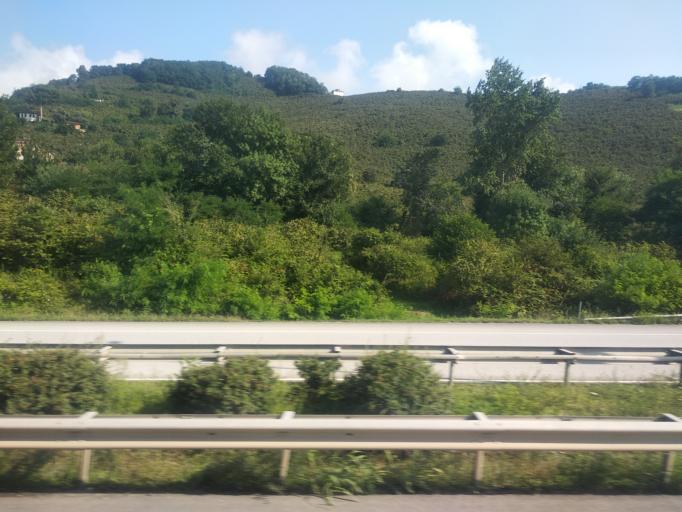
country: TR
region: Ordu
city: Ordu
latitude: 41.0128
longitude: 37.8354
